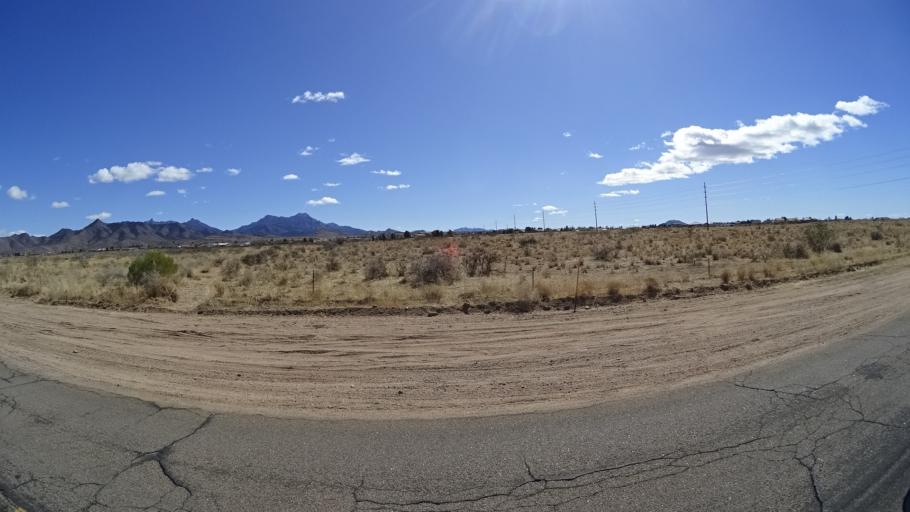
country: US
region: Arizona
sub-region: Mohave County
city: Kingman
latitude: 35.2012
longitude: -113.9873
